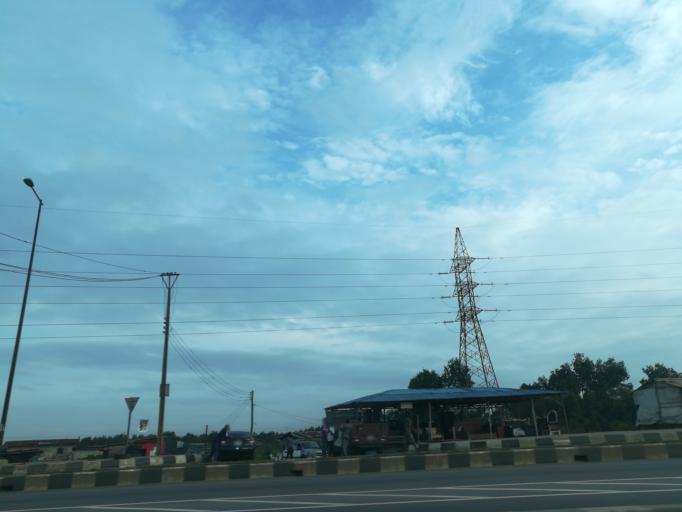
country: NG
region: Lagos
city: Ebute Ikorodu
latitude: 6.6091
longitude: 3.4387
